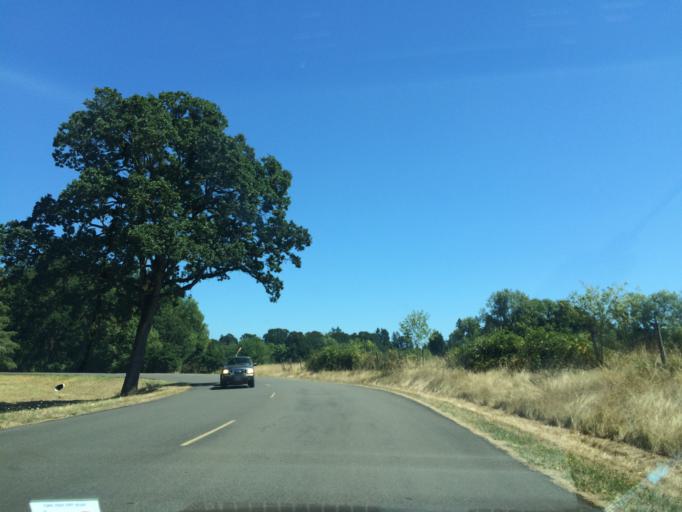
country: US
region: Oregon
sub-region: Yamhill County
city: Newberg
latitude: 45.2489
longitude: -122.8858
